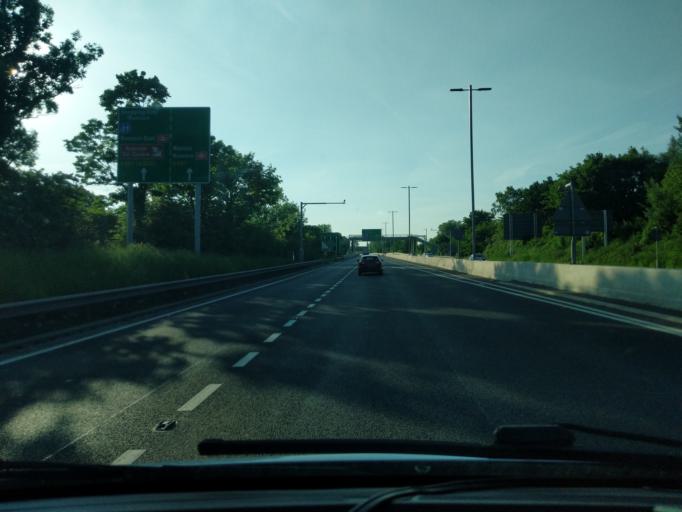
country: GB
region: England
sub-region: Borough of Halton
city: Halton
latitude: 53.3150
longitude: -2.7090
